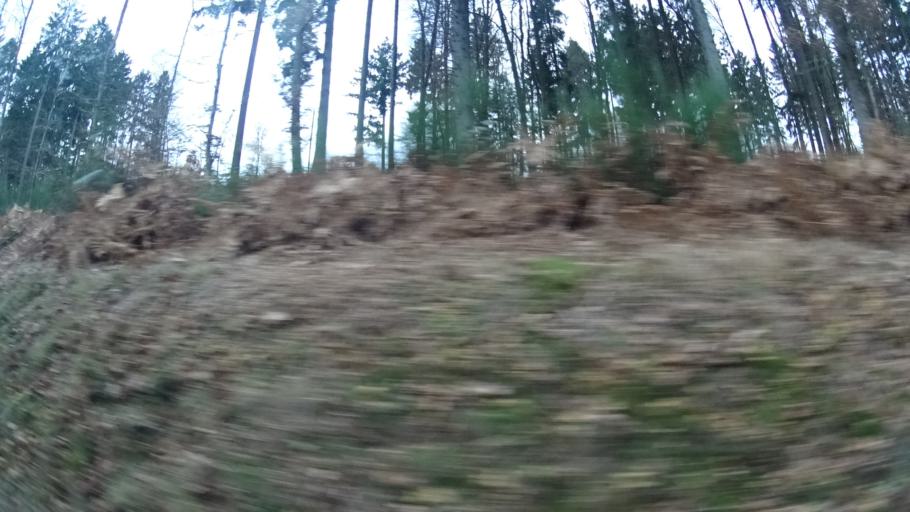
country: DE
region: Baden-Wuerttemberg
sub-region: Karlsruhe Region
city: Heddesbach
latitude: 49.4957
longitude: 8.8210
